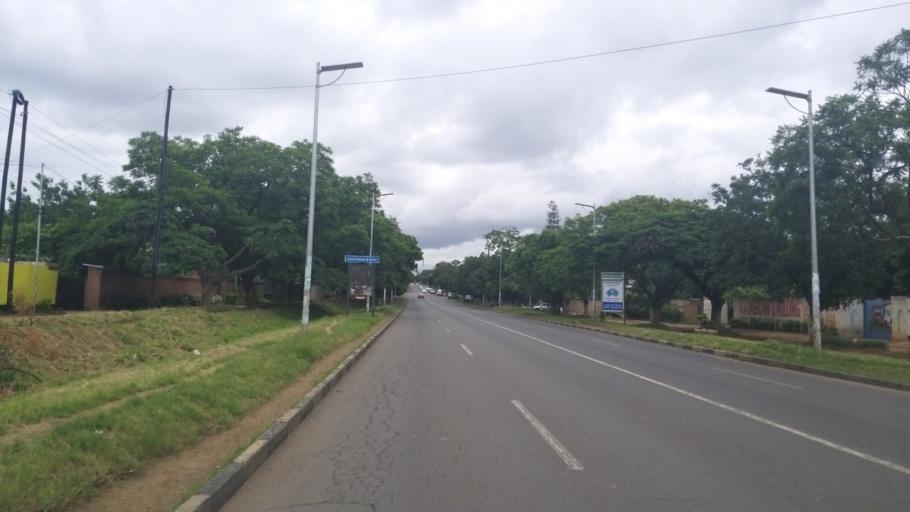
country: ZM
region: Lusaka
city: Lusaka
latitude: -15.4212
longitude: 28.2982
